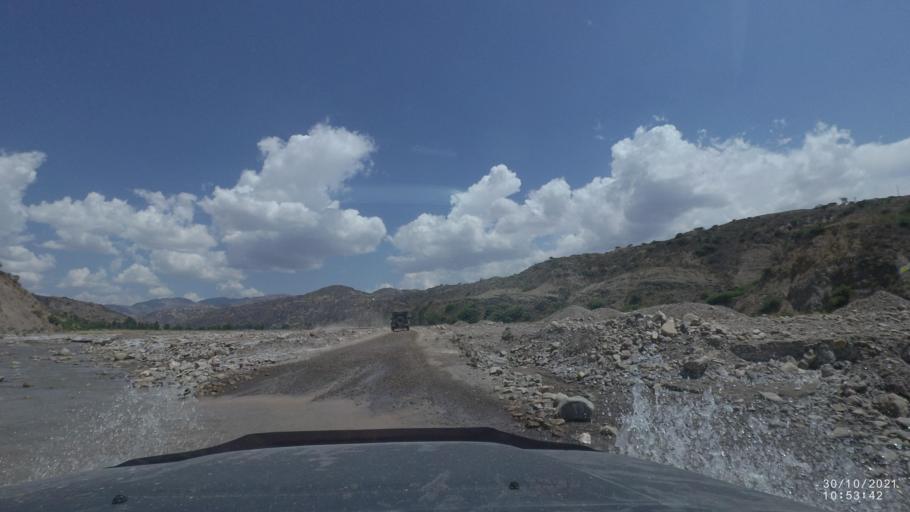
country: BO
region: Cochabamba
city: Sipe Sipe
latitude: -17.5479
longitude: -66.4834
